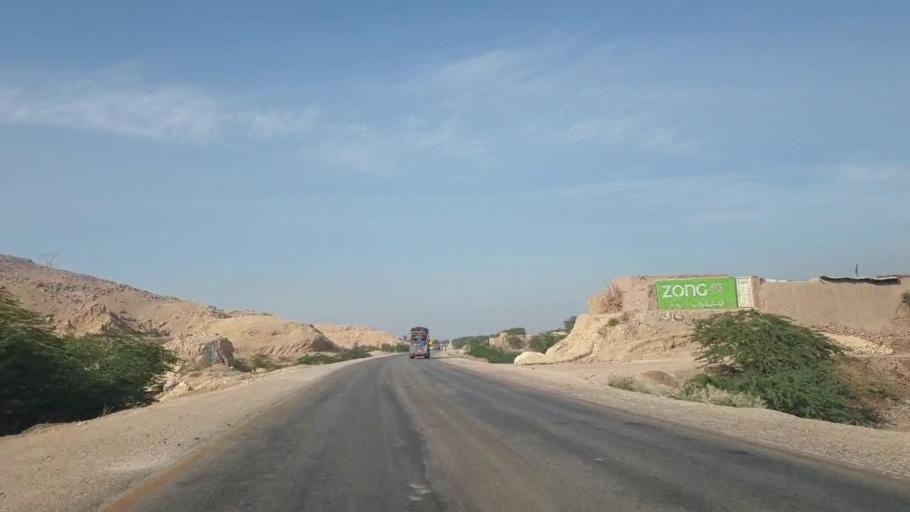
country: PK
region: Sindh
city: Sehwan
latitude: 26.3049
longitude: 67.8934
